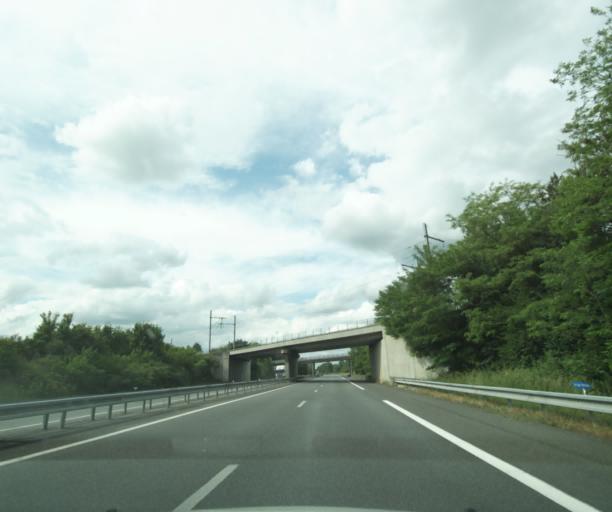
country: FR
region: Centre
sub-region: Departement du Cher
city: Foecy
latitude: 47.1627
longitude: 2.1825
